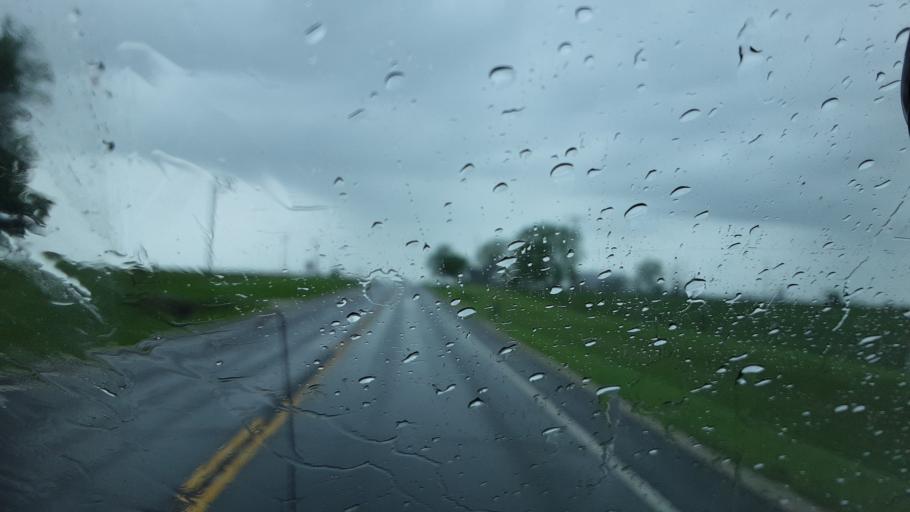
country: US
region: Missouri
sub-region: Monroe County
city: Paris
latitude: 39.4801
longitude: -92.1691
